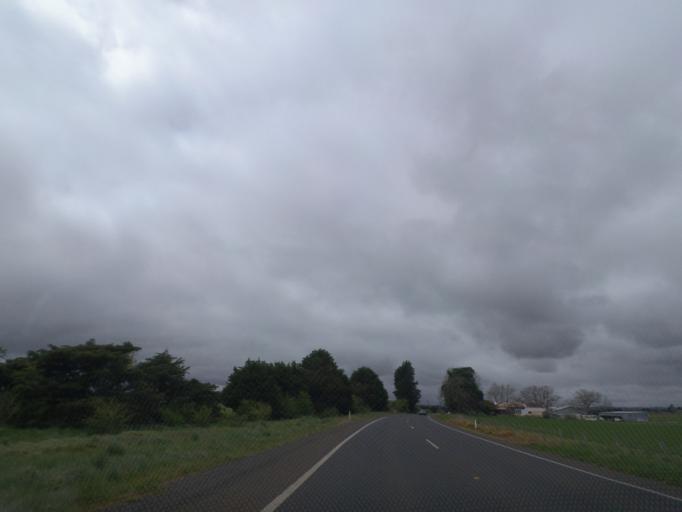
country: AU
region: Victoria
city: Brown Hill
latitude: -37.4075
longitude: 143.9628
